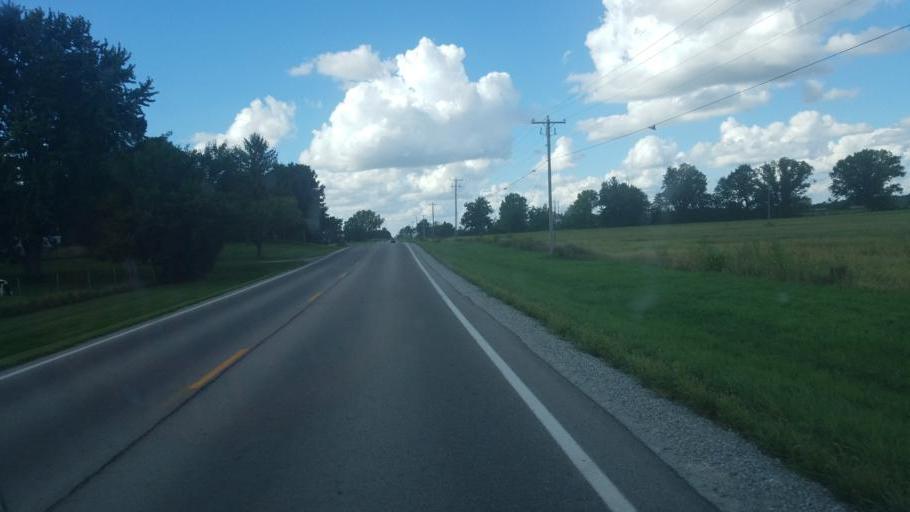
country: US
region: Ohio
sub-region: Hardin County
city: Kenton
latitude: 40.5720
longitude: -83.5518
